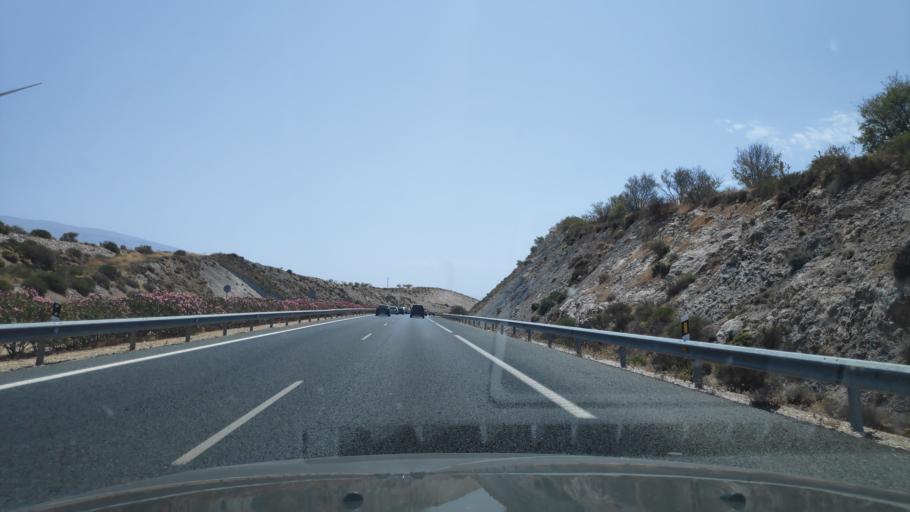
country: ES
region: Andalusia
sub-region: Provincia de Granada
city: Padul
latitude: 37.0037
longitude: -3.6352
